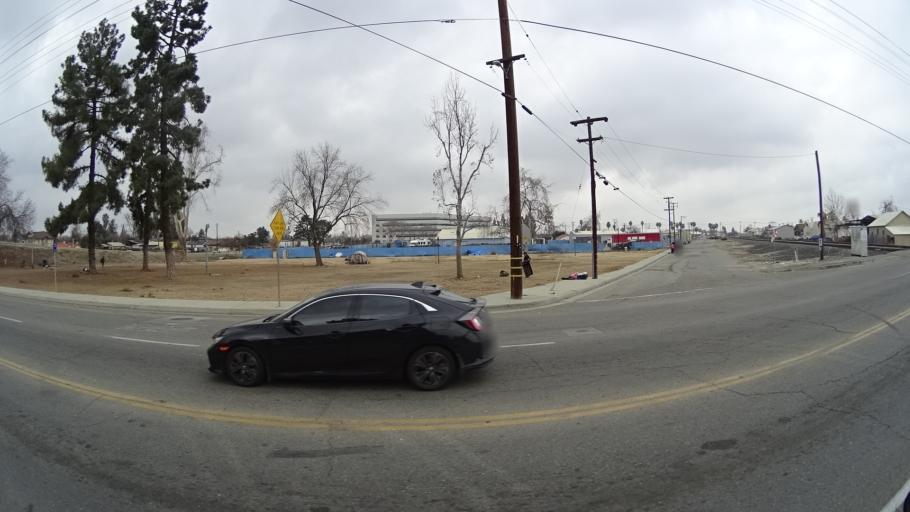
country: US
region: California
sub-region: Kern County
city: Bakersfield
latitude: 35.3836
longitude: -119.0105
